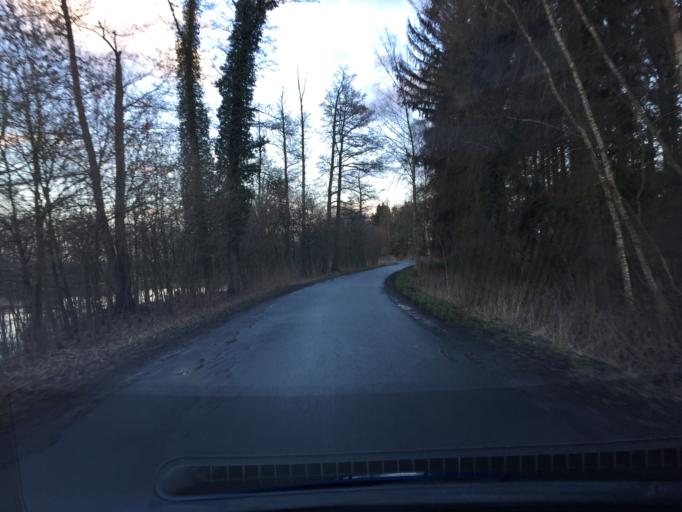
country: DE
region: Lower Saxony
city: Ludersburg
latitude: 53.3242
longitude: 10.5678
